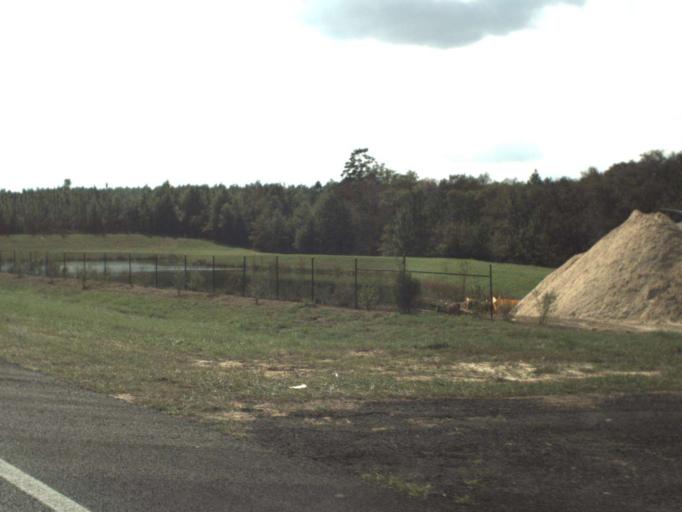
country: US
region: Florida
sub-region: Bay County
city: Laguna Beach
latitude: 30.5223
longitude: -85.8409
